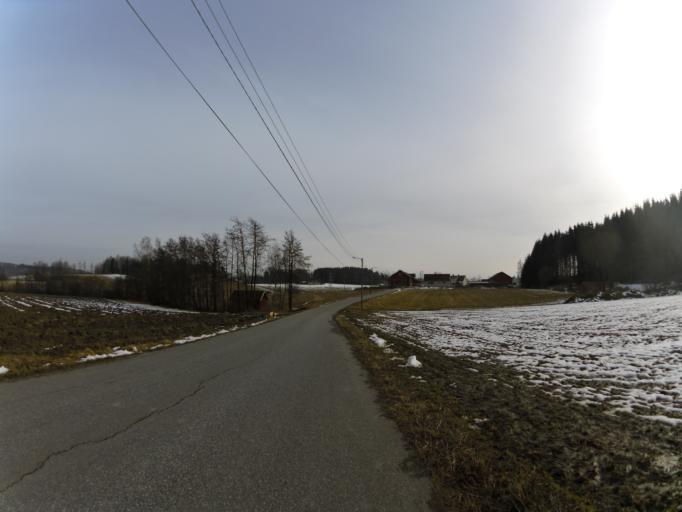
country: NO
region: Ostfold
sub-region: Fredrikstad
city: Fredrikstad
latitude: 59.2757
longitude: 11.0032
